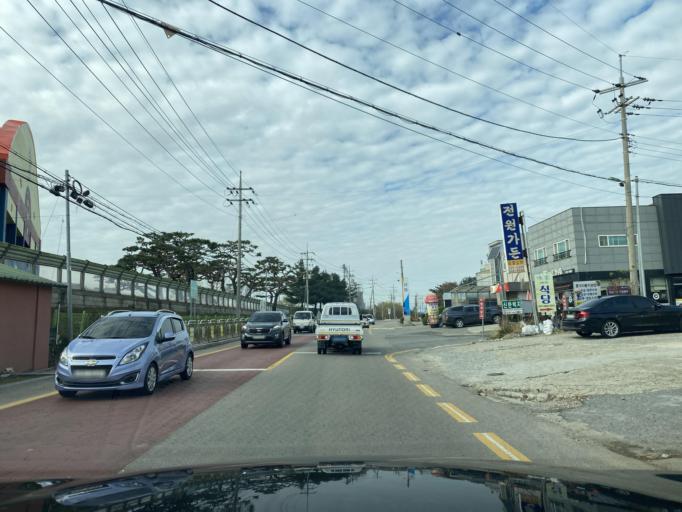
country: KR
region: Chungcheongnam-do
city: Yesan
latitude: 36.6883
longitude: 126.7948
